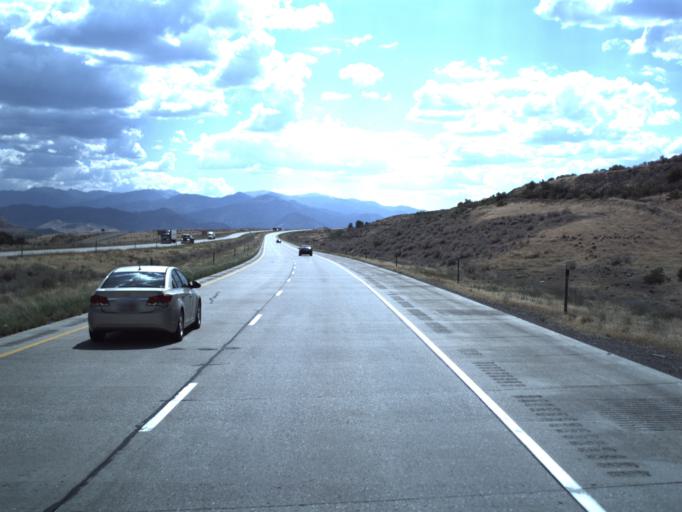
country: US
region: Utah
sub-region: Sevier County
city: Monroe
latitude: 38.6693
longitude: -112.1699
